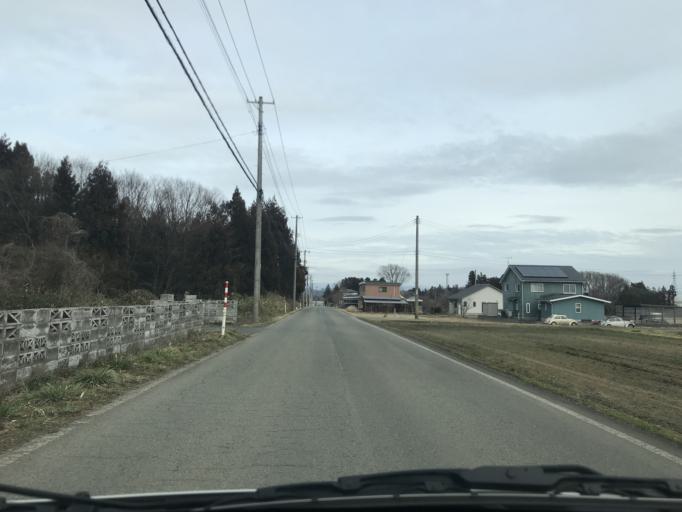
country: JP
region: Iwate
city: Kitakami
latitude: 39.2522
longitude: 141.0835
